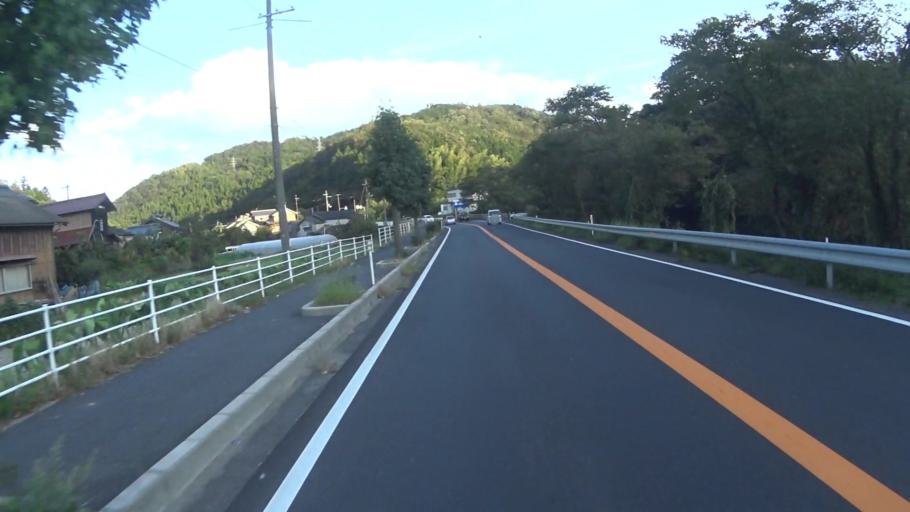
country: JP
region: Kyoto
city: Miyazu
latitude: 35.5627
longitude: 135.0969
